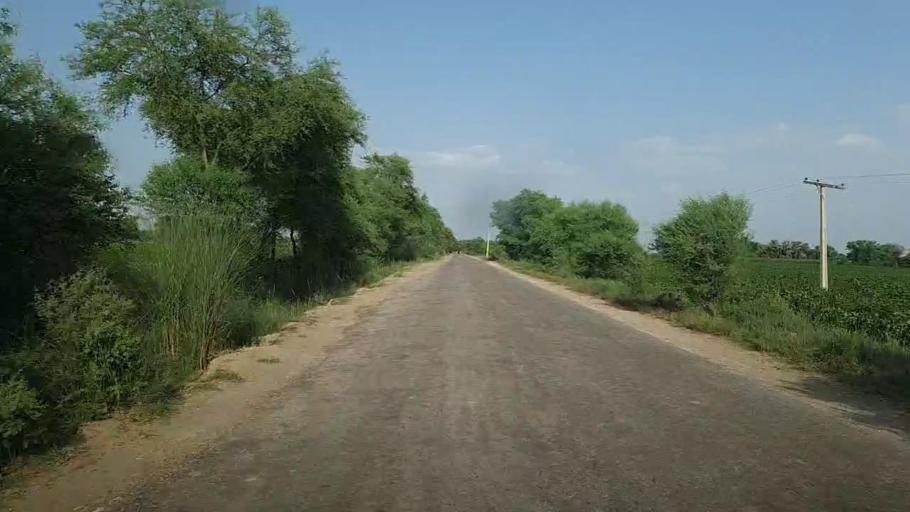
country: PK
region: Sindh
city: Khairpur
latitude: 28.0758
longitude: 69.8079
